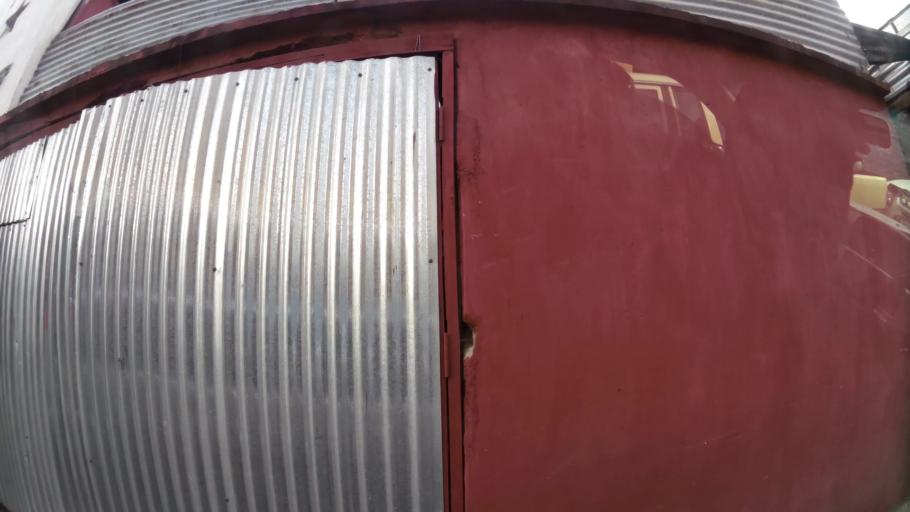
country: GT
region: Quiche
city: Chichicastenango
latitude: 14.9444
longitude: -91.1137
